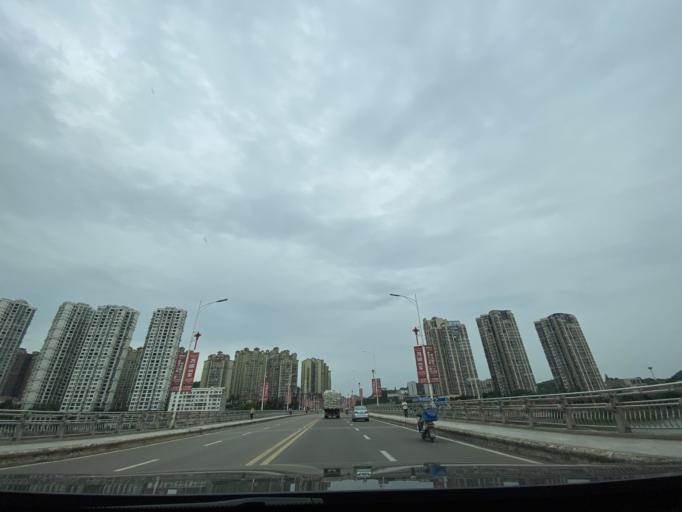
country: CN
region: Sichuan
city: Jiancheng
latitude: 30.3902
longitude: 104.5569
